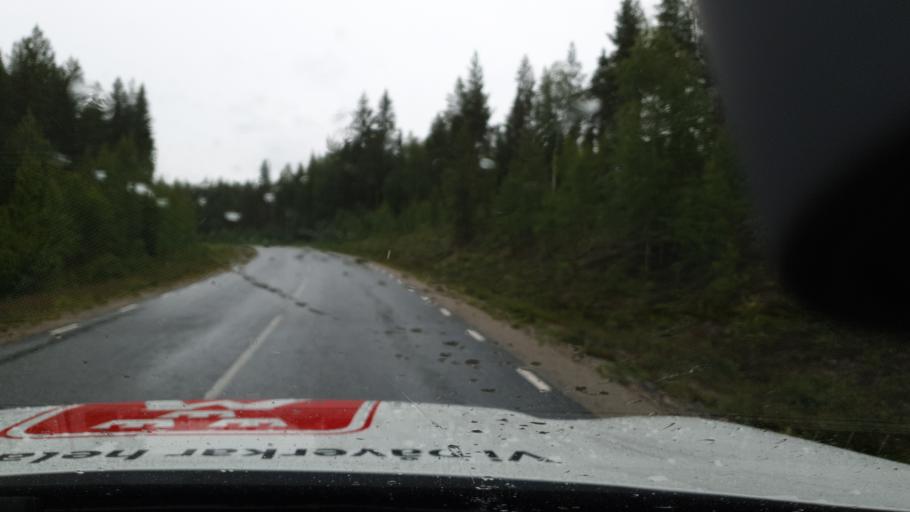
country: SE
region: Vaesterbotten
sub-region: Vindelns Kommun
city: Vindeln
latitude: 64.4572
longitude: 19.7565
